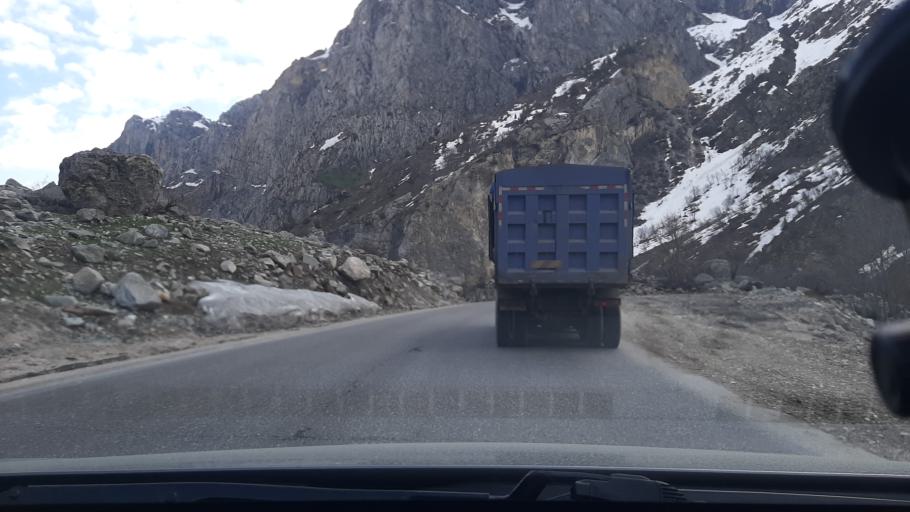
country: TJ
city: Tagob
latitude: 39.0001
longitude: 68.7688
